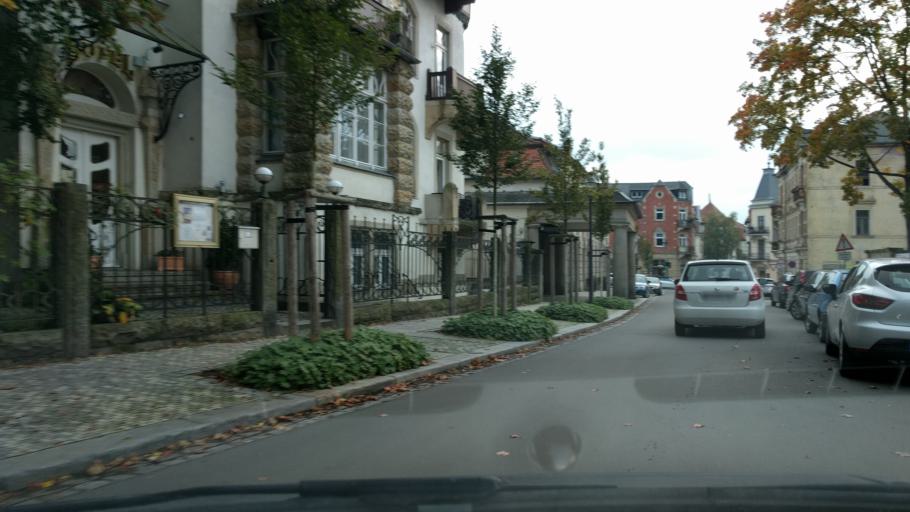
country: DE
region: Saxony
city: Albertstadt
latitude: 51.0646
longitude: 13.8216
